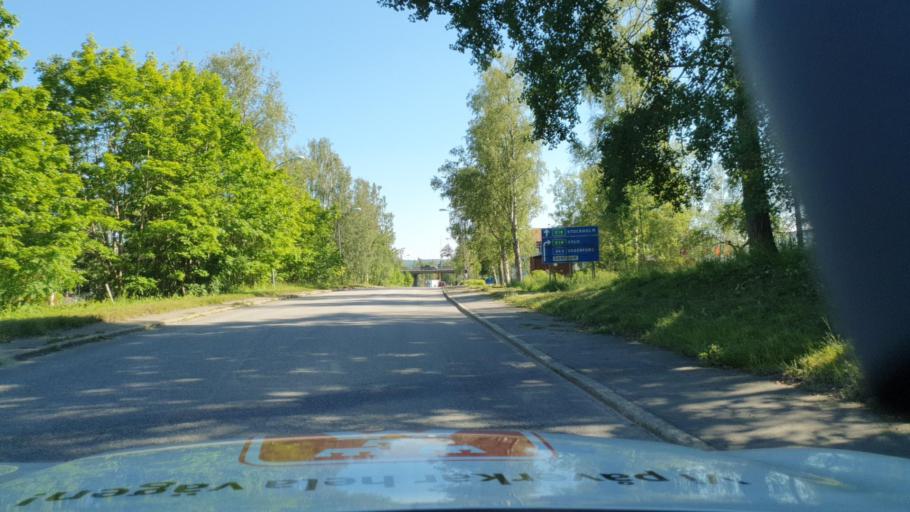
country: SE
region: OErebro
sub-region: Karlskoga Kommun
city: Karlskoga
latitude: 59.3329
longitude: 14.5489
